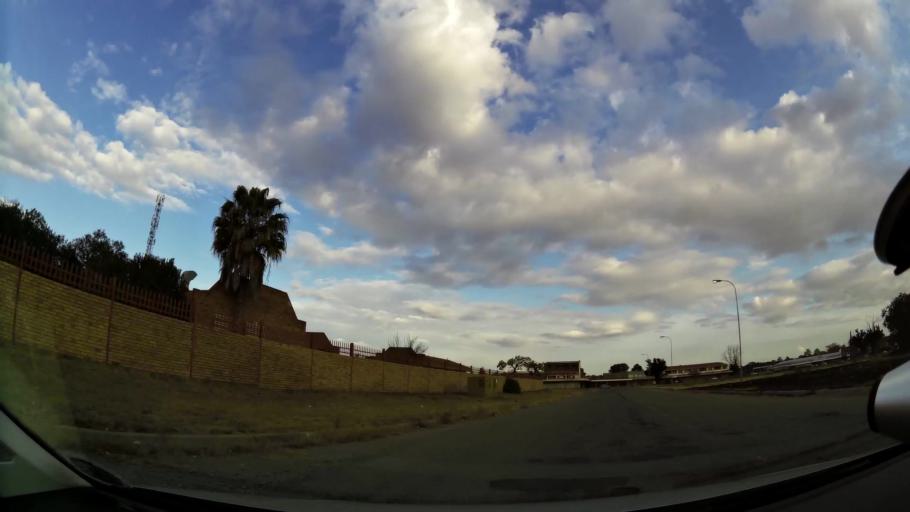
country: ZA
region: Orange Free State
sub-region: Lejweleputswa District Municipality
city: Welkom
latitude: -27.9884
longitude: 26.7127
